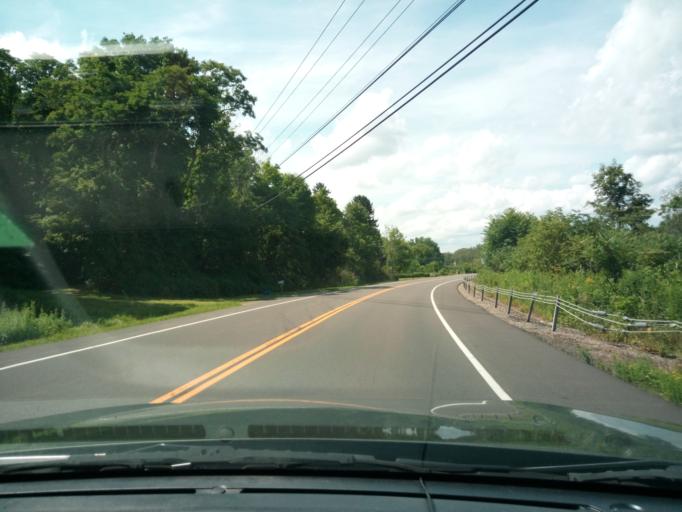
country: US
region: New York
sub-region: Chemung County
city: Southport
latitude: 42.0224
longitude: -76.7400
